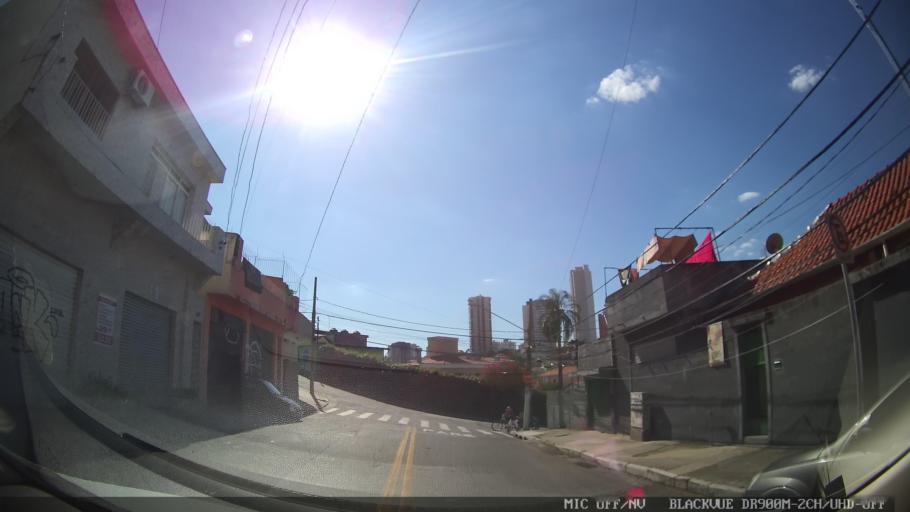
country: BR
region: Sao Paulo
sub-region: Sao Paulo
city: Sao Paulo
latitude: -23.4883
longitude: -46.6410
